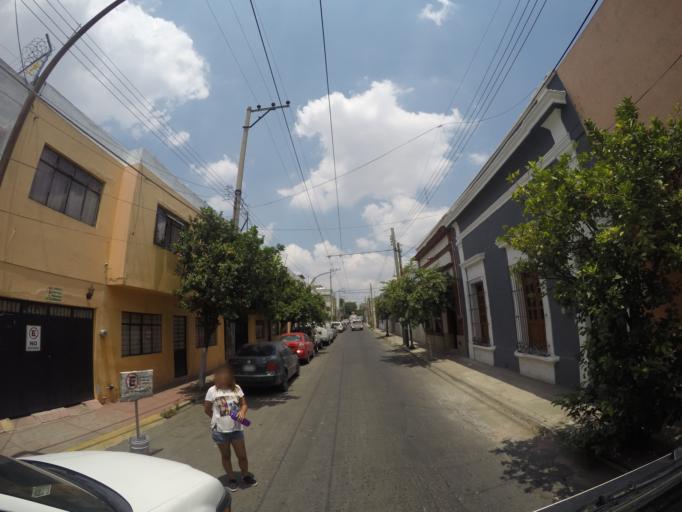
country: MX
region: Jalisco
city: Guadalajara
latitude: 20.6781
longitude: -103.3556
